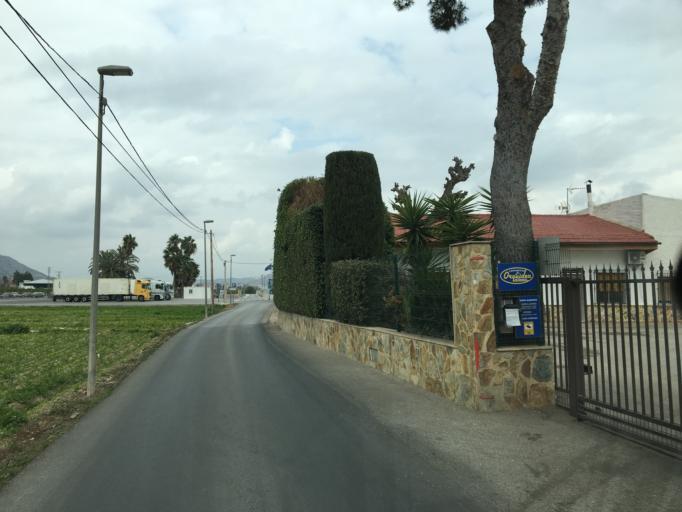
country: ES
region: Murcia
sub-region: Murcia
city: Santomera
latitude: 38.0432
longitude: -1.0313
